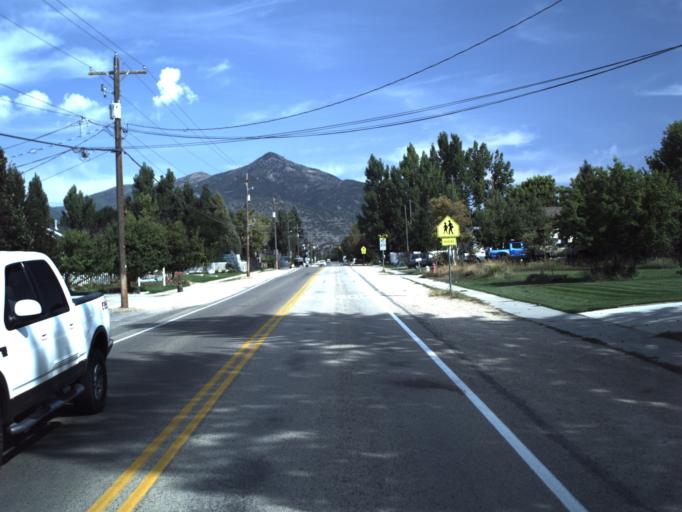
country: US
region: Utah
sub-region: Wasatch County
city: Midway
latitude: 40.5090
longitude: -111.4723
